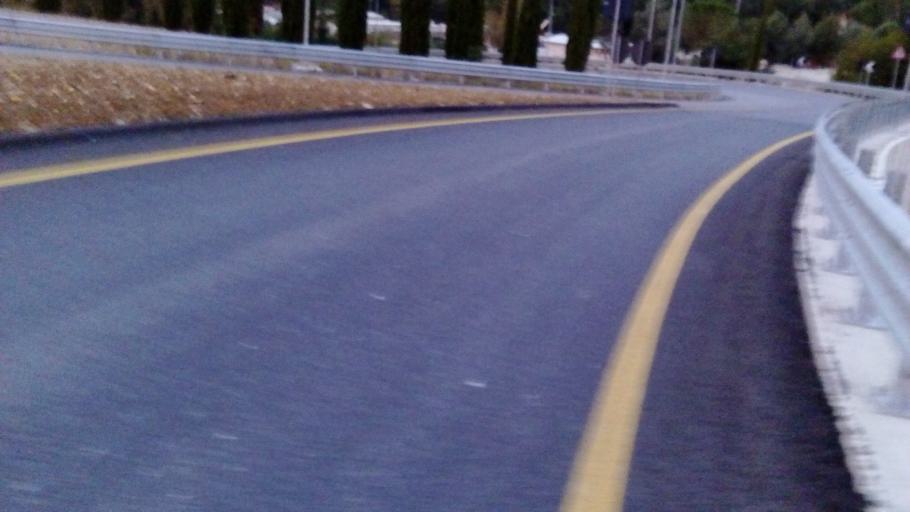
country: IT
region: Tuscany
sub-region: Provincia di Grosseto
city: Civitella Marittima
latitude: 43.0290
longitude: 11.2775
